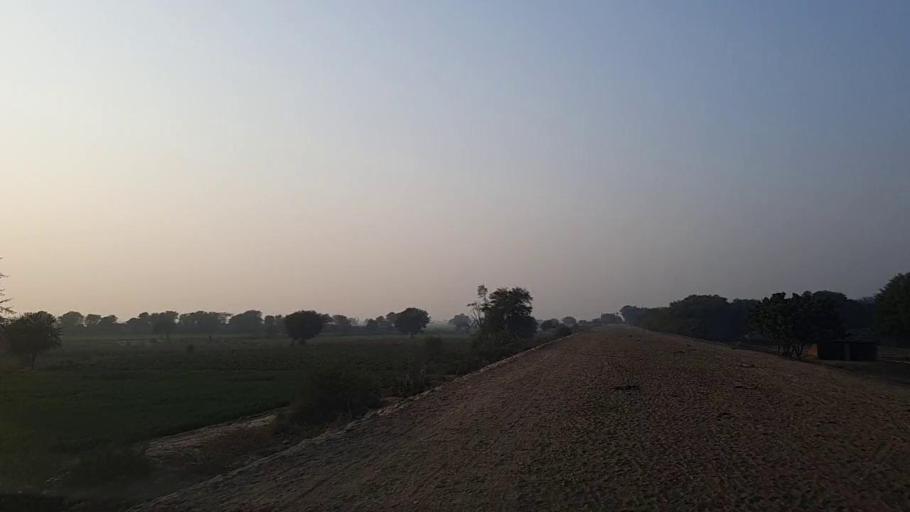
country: PK
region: Sindh
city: Sann
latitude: 26.1755
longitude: 68.0996
